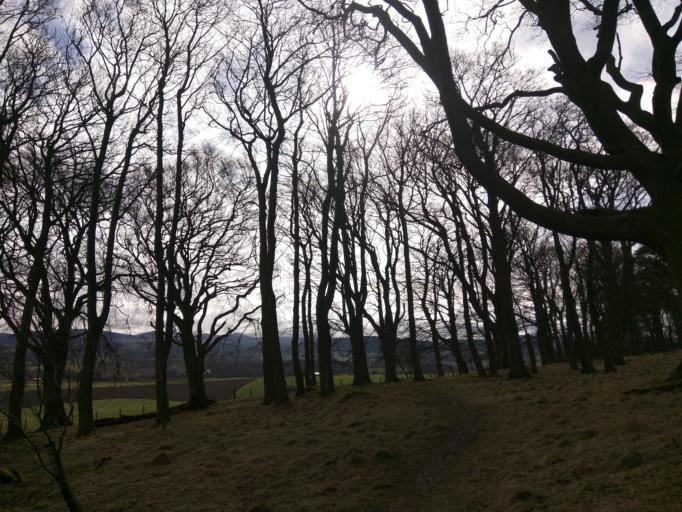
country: GB
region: Scotland
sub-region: Edinburgh
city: Ratho
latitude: 55.9133
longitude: -3.3944
